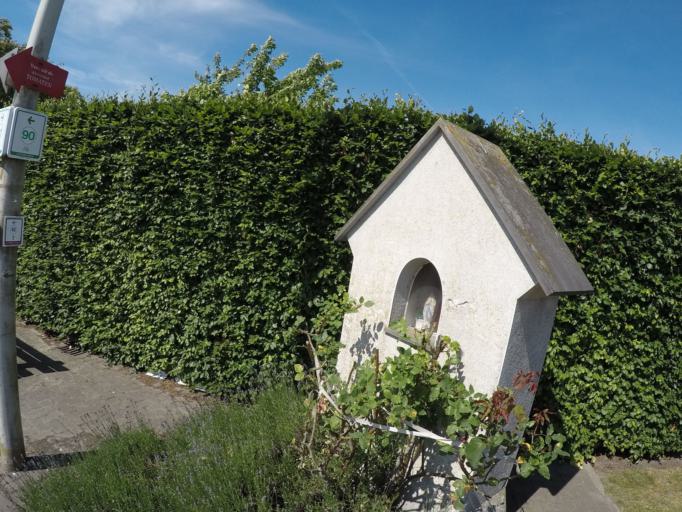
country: BE
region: Flanders
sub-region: Provincie Antwerpen
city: Wuustwezel
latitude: 51.4270
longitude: 4.6018
